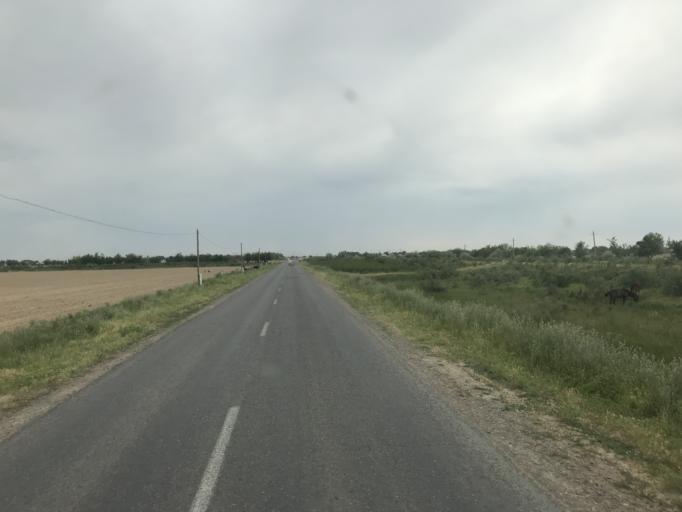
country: KZ
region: Ongtustik Qazaqstan
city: Asykata
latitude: 40.9224
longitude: 68.4010
